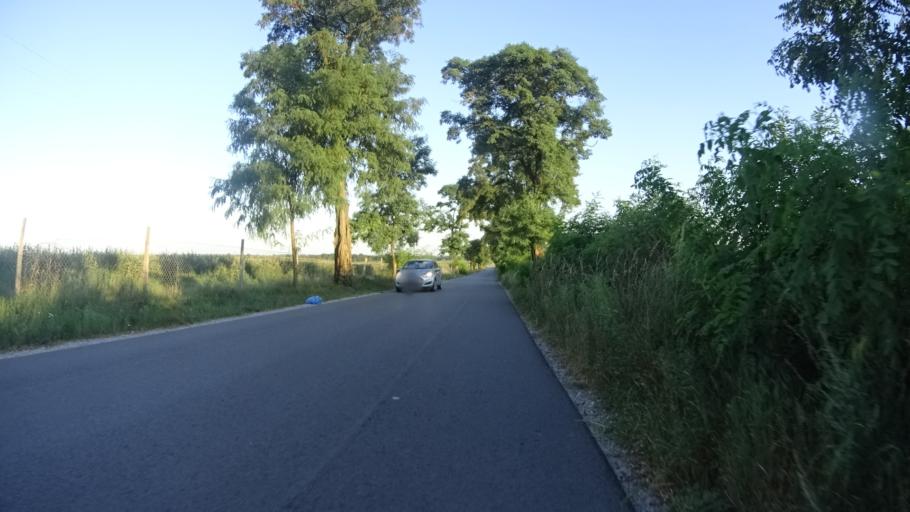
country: PL
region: Masovian Voivodeship
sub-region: Powiat grojecki
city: Goszczyn
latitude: 51.6870
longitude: 20.8208
